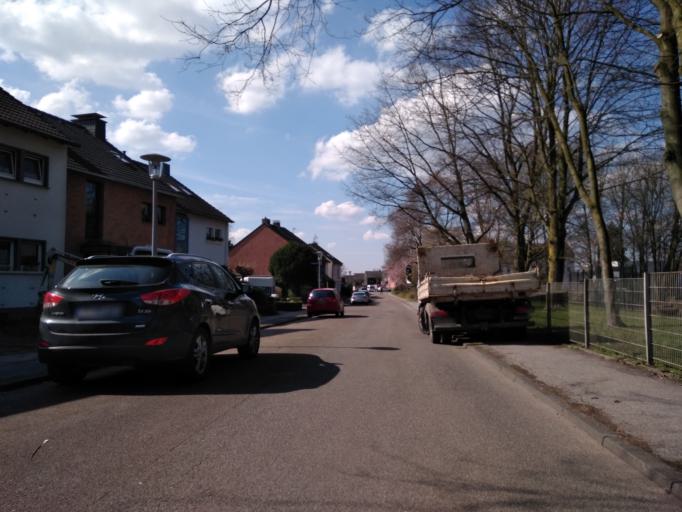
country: DE
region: North Rhine-Westphalia
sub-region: Regierungsbezirk Munster
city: Gladbeck
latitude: 51.5851
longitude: 7.0027
